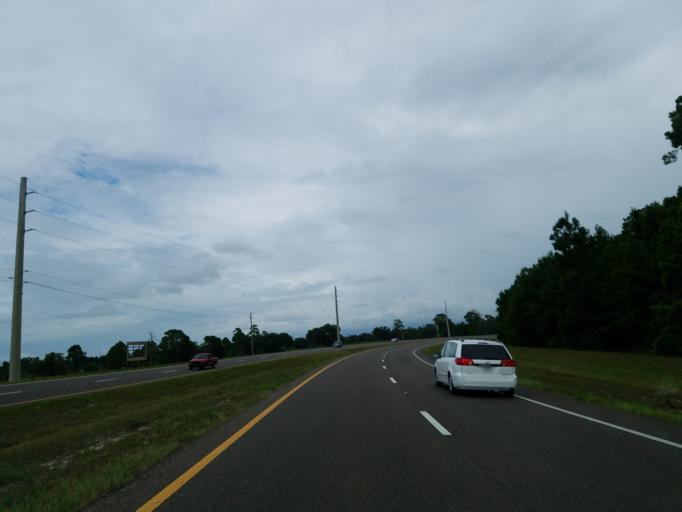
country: US
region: Florida
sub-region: Sumter County
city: Wildwood
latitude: 28.8797
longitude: -82.1265
